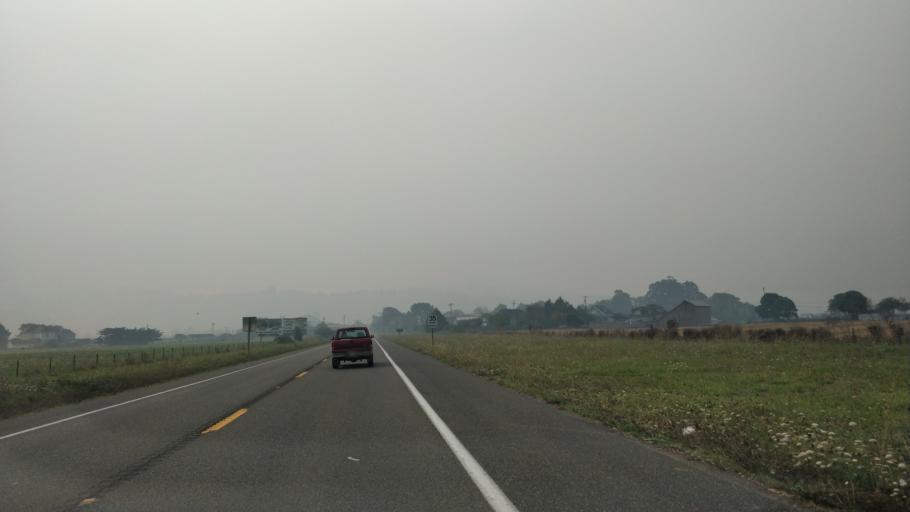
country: US
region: California
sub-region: Humboldt County
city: Ferndale
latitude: 40.5920
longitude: -124.2518
